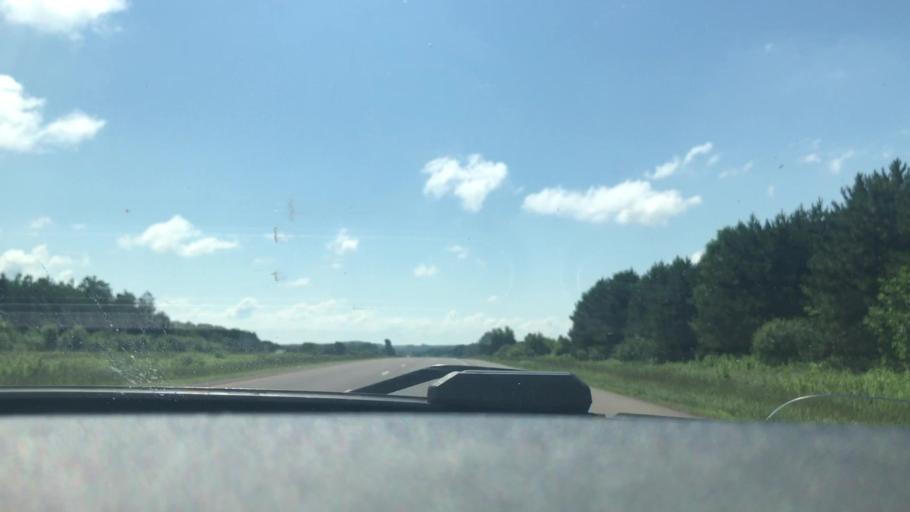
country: US
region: Wisconsin
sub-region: Chippewa County
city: Bloomer
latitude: 45.0863
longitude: -91.4863
